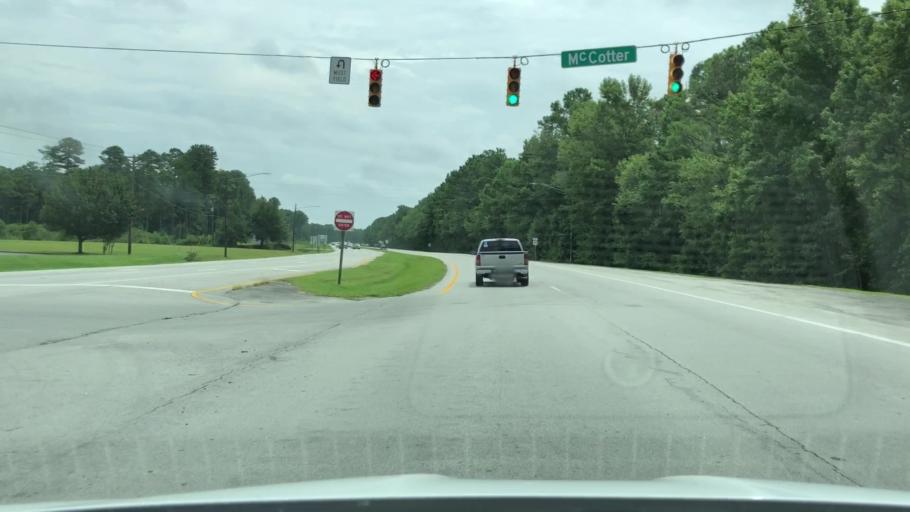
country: US
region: North Carolina
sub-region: Craven County
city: Havelock
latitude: 34.8558
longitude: -76.8951
